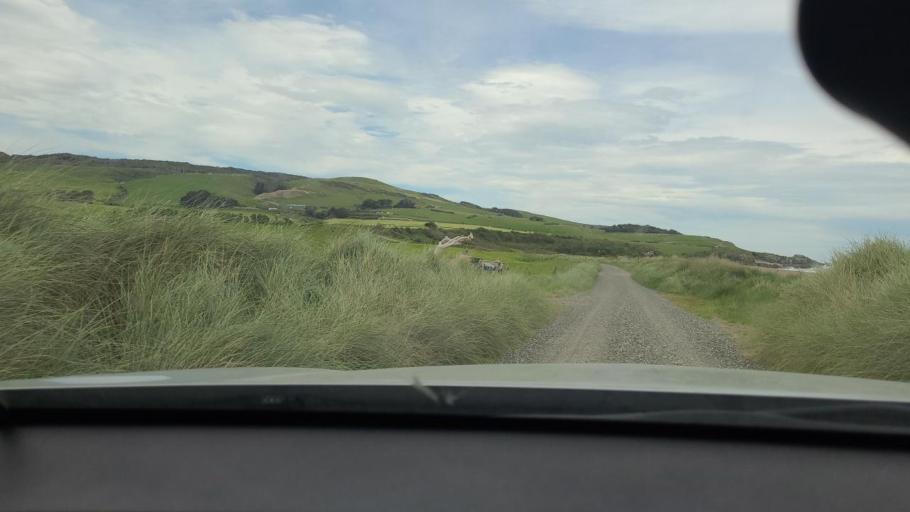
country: NZ
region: Southland
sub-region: Southland District
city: Riverton
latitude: -46.3596
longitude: 167.9411
